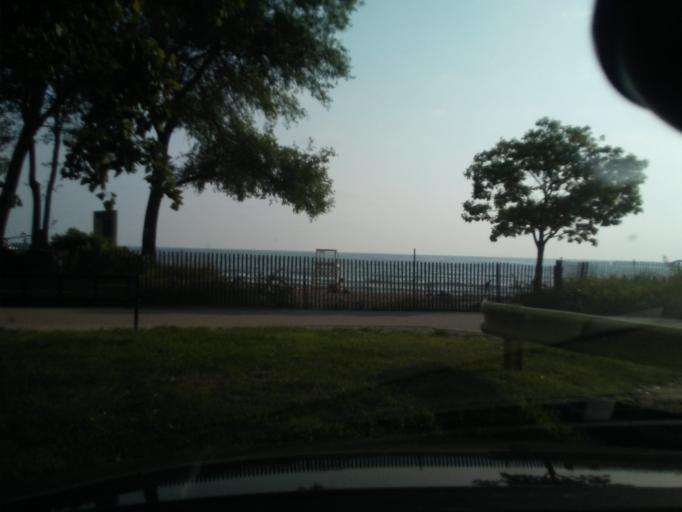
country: US
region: Illinois
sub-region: Cook County
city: Evanston
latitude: 42.0426
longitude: -87.6717
